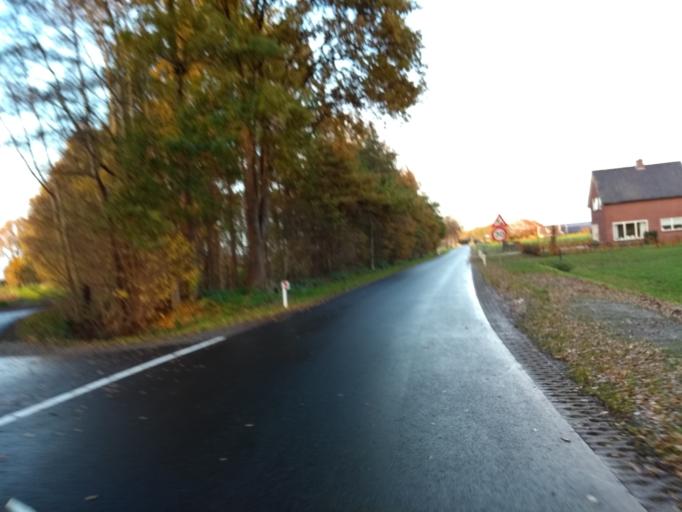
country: NL
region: Overijssel
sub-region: Gemeente Almelo
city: Almelo
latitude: 52.3881
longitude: 6.6875
